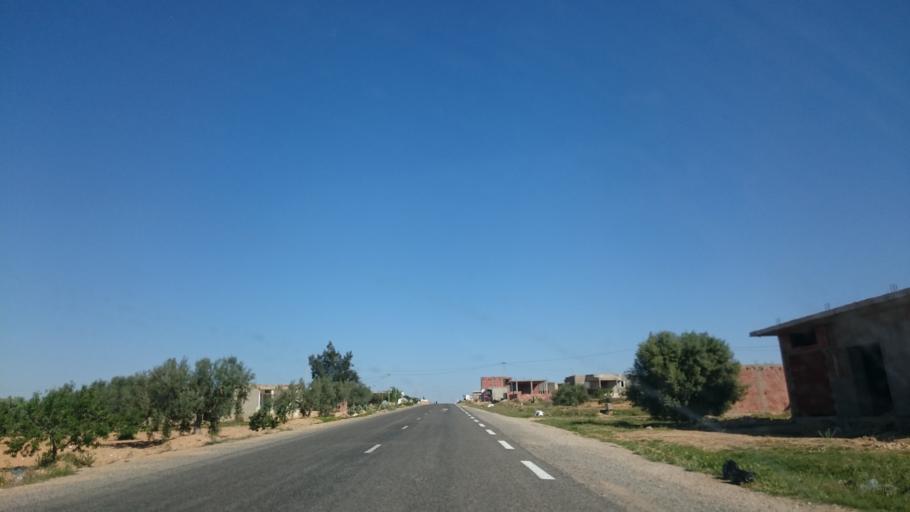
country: TN
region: Safaqis
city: Sfax
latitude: 34.7776
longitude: 10.5059
